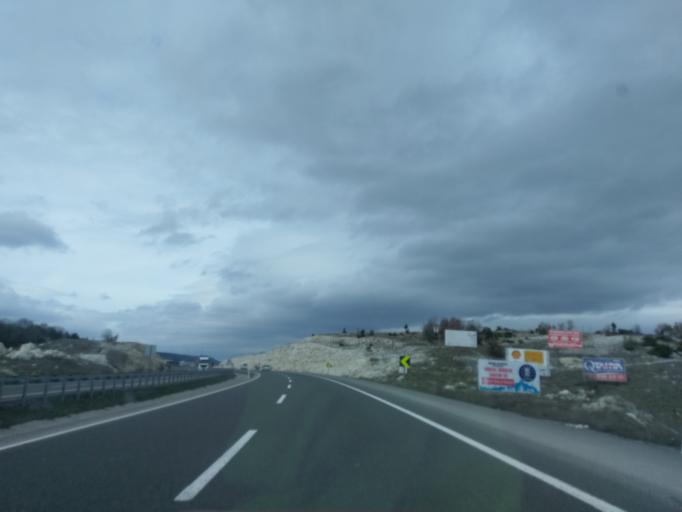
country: TR
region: Kuetahya
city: Kutahya
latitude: 39.3741
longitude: 30.0647
